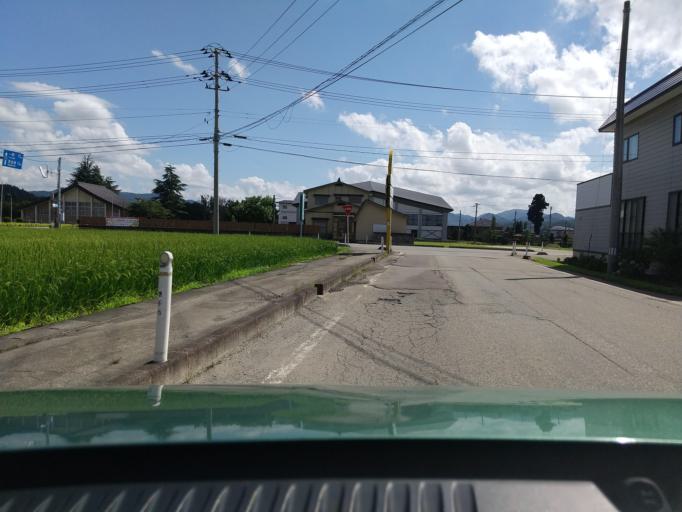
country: JP
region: Akita
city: Yuzawa
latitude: 39.2039
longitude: 140.5564
